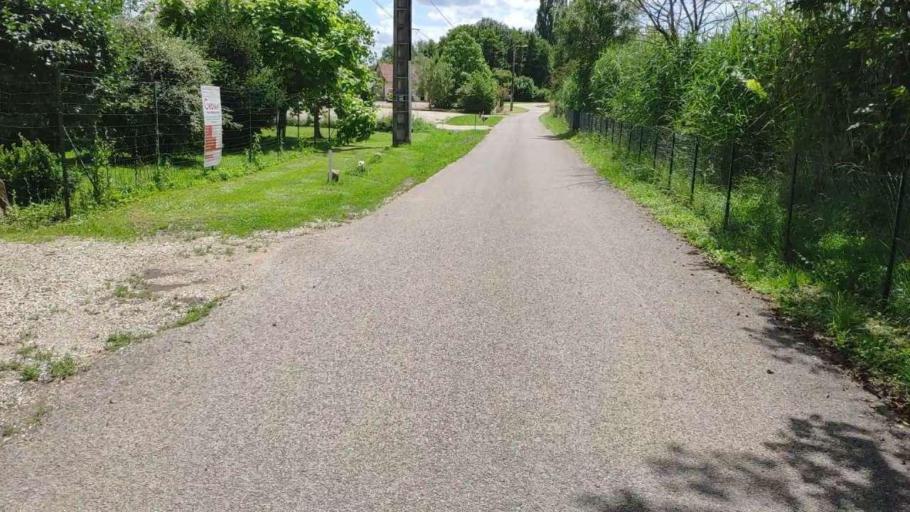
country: FR
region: Franche-Comte
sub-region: Departement du Jura
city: Bletterans
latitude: 46.8450
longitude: 5.4785
